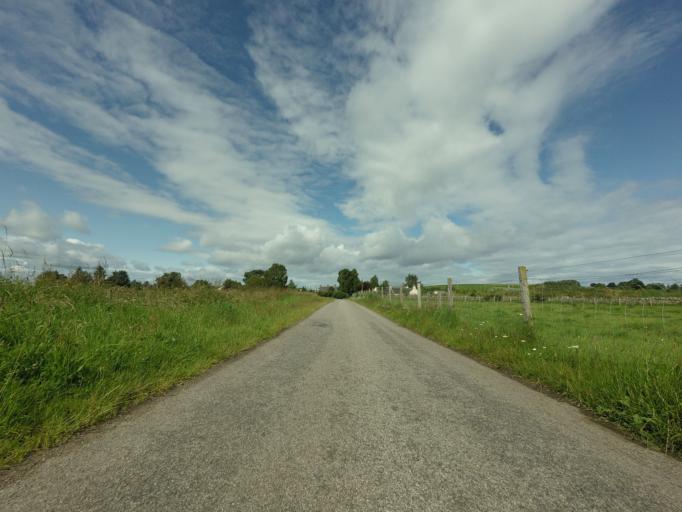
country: GB
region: Scotland
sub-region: Moray
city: Burghead
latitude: 57.6545
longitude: -3.4752
